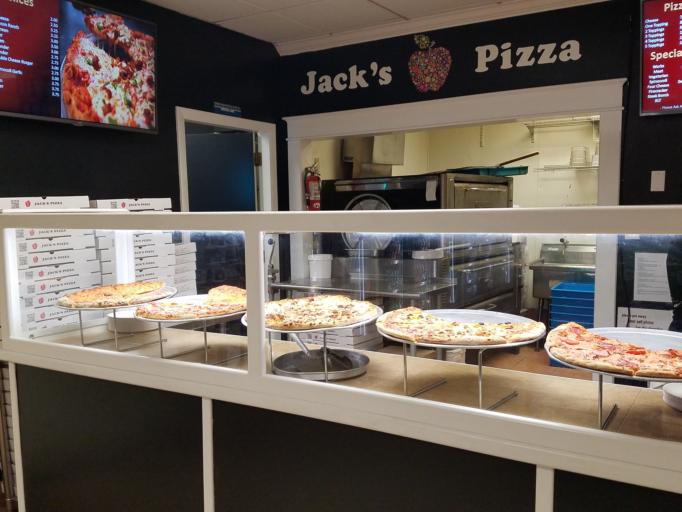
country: US
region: New Hampshire
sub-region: Strafford County
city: New Durham
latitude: 43.4522
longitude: -71.2126
